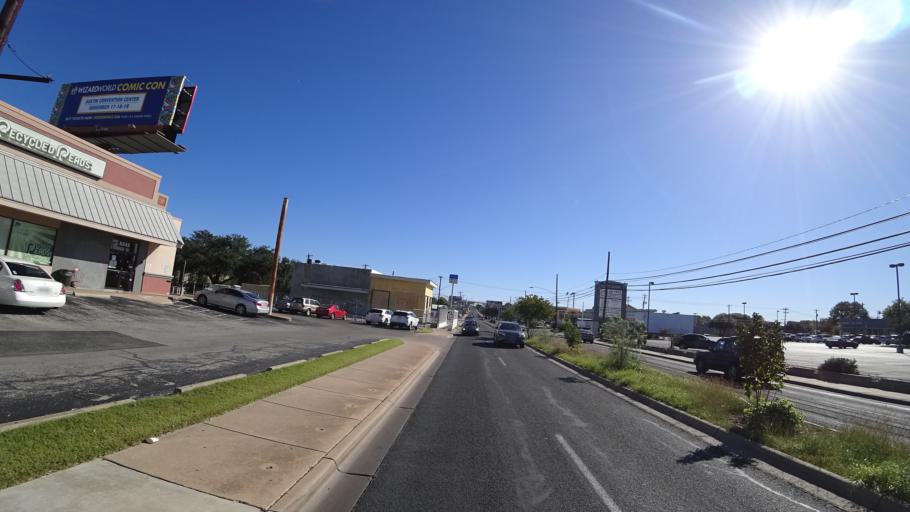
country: US
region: Texas
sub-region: Travis County
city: Austin
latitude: 30.3269
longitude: -97.7396
